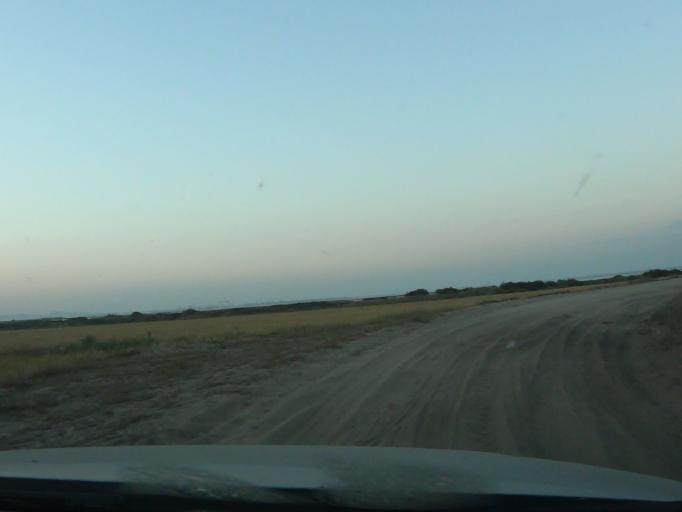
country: PT
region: Setubal
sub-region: Setubal
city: Setubal
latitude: 38.4062
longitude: -8.7658
